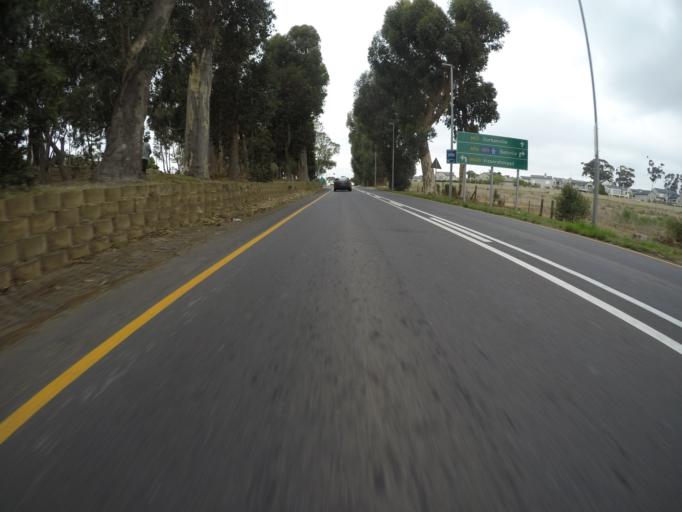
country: ZA
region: Western Cape
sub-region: City of Cape Town
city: Kraaifontein
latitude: -33.8436
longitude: 18.6333
